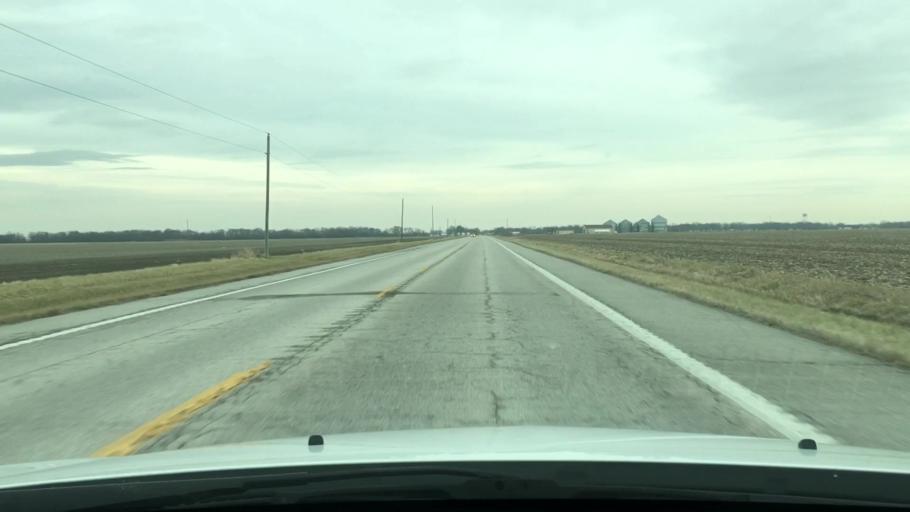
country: US
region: Missouri
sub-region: Audrain County
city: Vandalia
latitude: 39.2800
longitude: -91.6050
